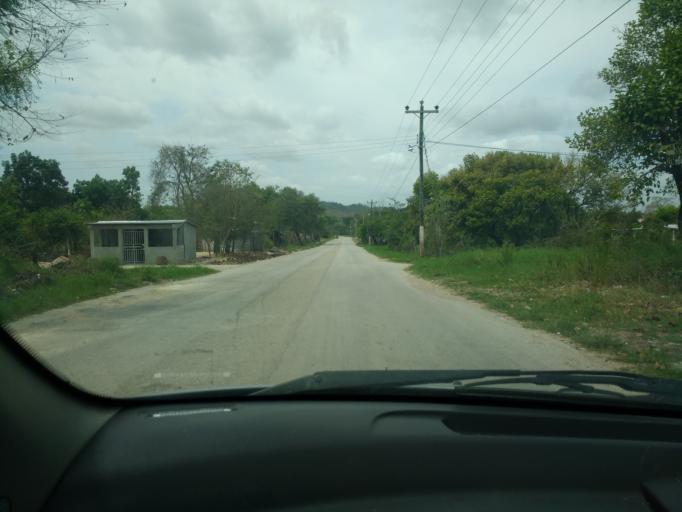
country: GT
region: Peten
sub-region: Municipio de San Benito
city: San Benito
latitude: 16.9201
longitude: -89.9271
